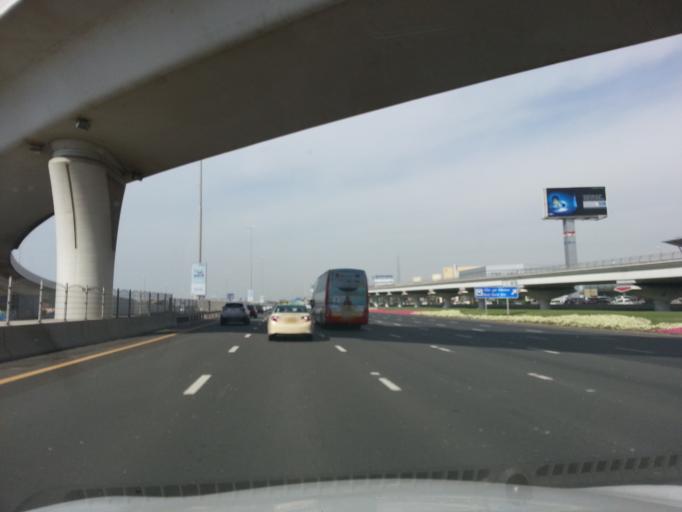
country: AE
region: Dubai
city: Dubai
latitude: 25.1396
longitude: 55.2179
